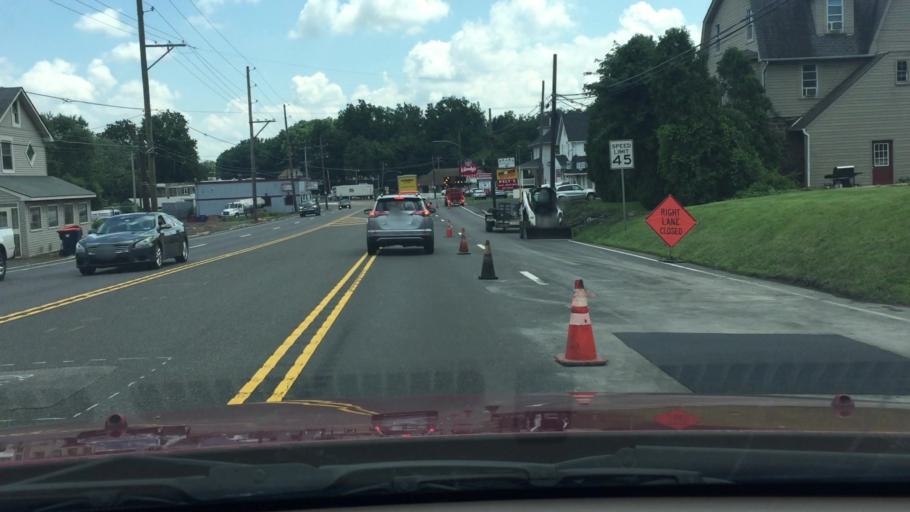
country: US
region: Pennsylvania
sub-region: Montgomery County
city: Horsham
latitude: 40.1816
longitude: -75.1312
